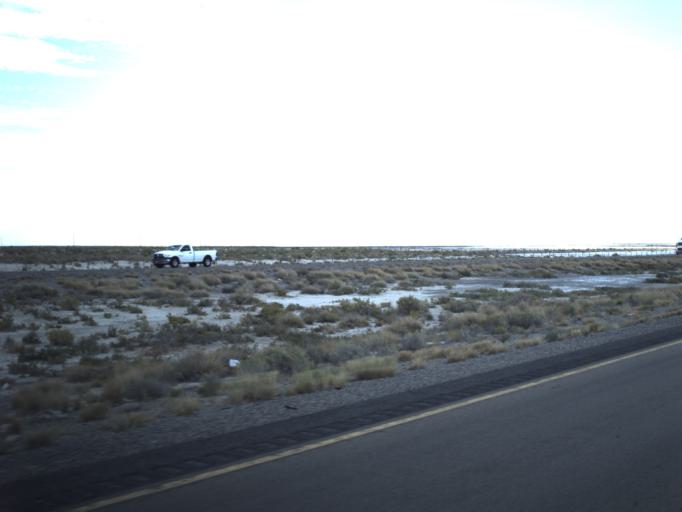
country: US
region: Utah
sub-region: Tooele County
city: Grantsville
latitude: 40.7567
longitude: -112.7635
